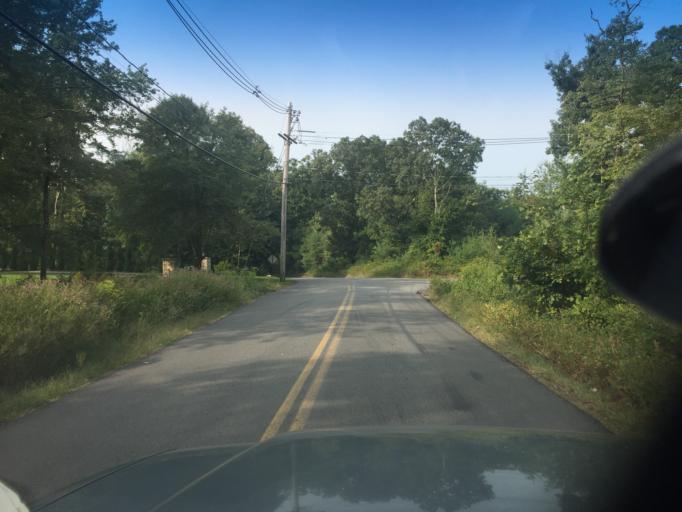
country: US
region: Massachusetts
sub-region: Norfolk County
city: Bellingham
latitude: 42.1315
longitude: -71.4661
